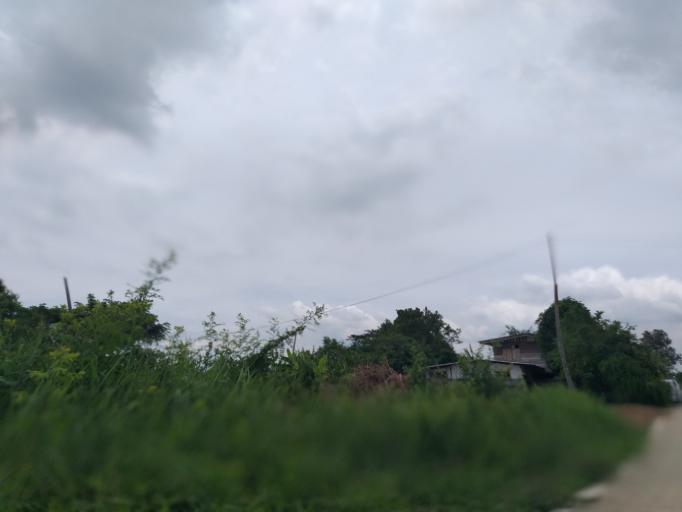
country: TH
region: Pathum Thani
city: Ban Lam Luk Ka
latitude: 13.9644
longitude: 100.8527
